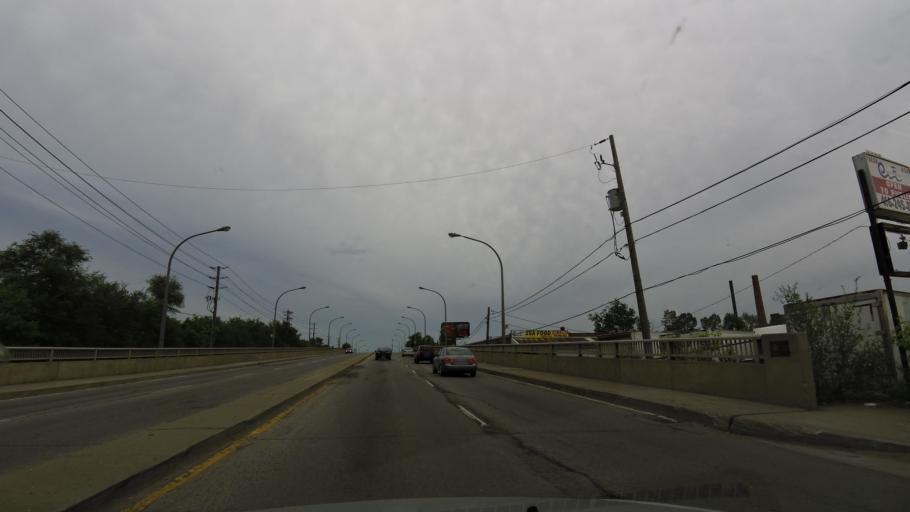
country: CA
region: Ontario
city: Etobicoke
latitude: 43.6966
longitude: -79.5022
